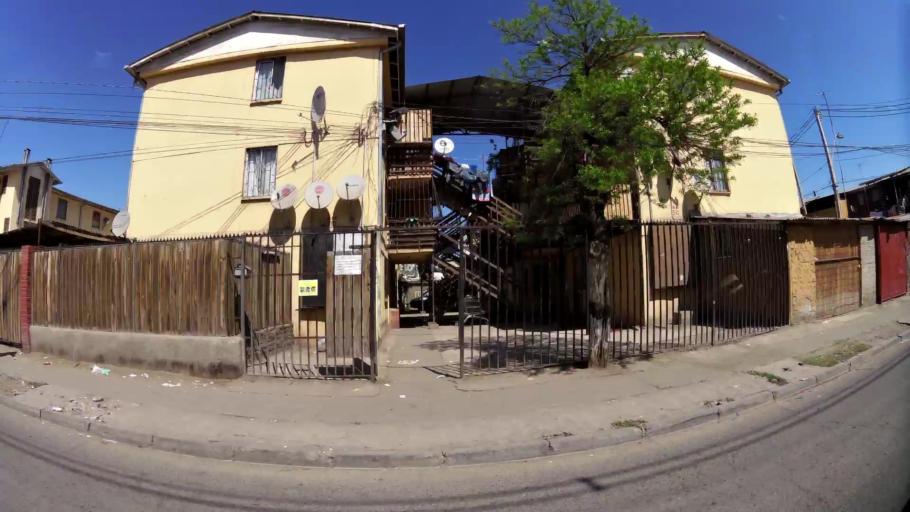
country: CL
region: Santiago Metropolitan
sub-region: Provincia de Santiago
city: Lo Prado
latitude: -33.3684
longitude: -70.7462
